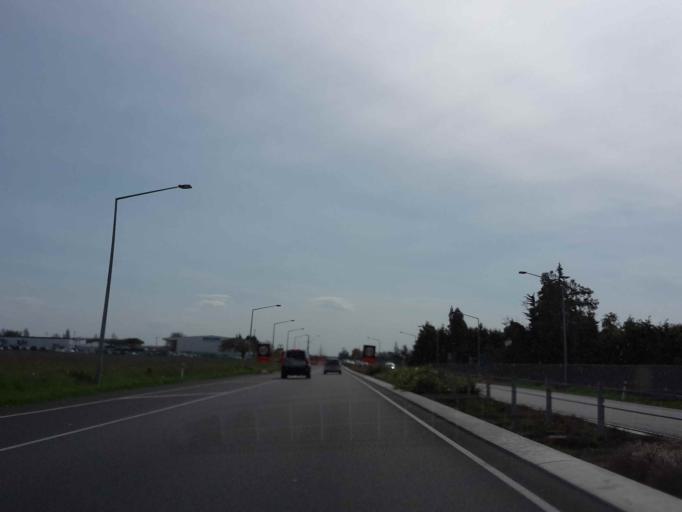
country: NZ
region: Canterbury
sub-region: Selwyn District
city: Prebbleton
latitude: -43.4997
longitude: 172.5460
